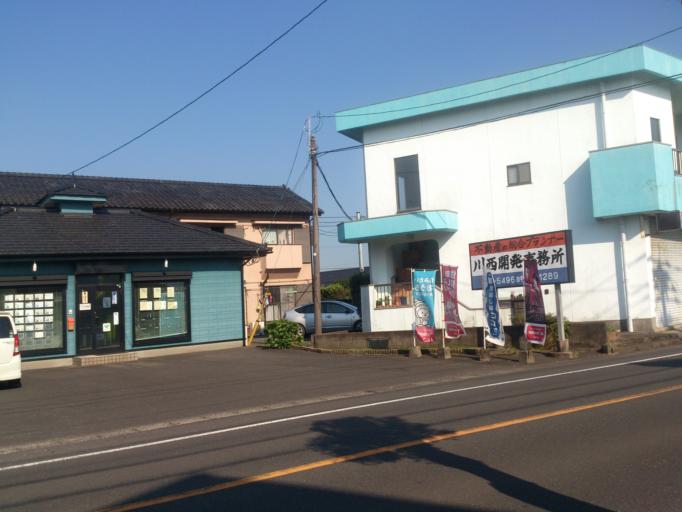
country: JP
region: Kagoshima
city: Kanoya
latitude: 31.3559
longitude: 130.8797
